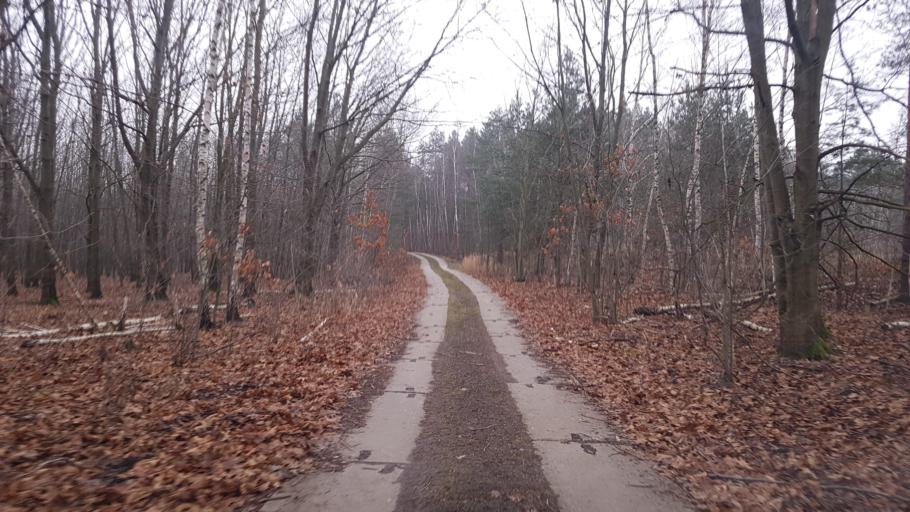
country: DE
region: Brandenburg
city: Plessa
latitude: 51.4935
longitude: 13.6366
